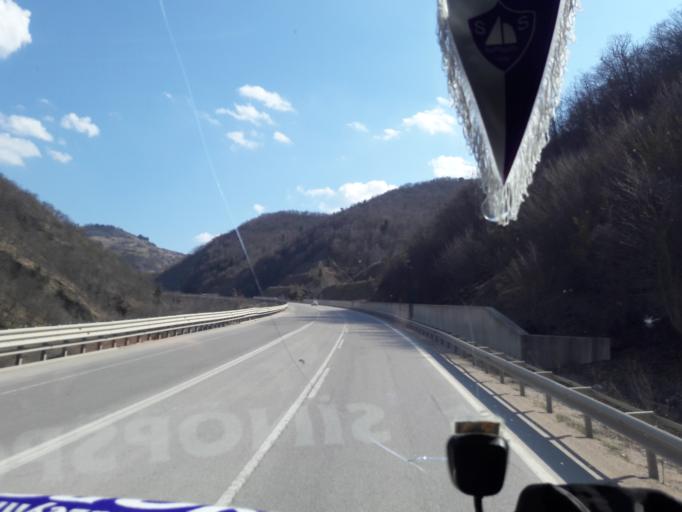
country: TR
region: Sinop
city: Erfelek
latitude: 41.6814
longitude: 34.9089
